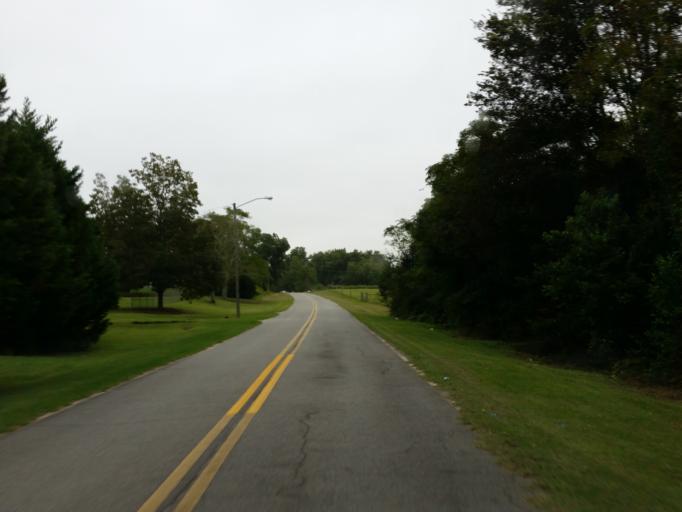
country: US
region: Georgia
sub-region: Dooly County
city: Unadilla
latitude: 32.2718
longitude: -83.7385
